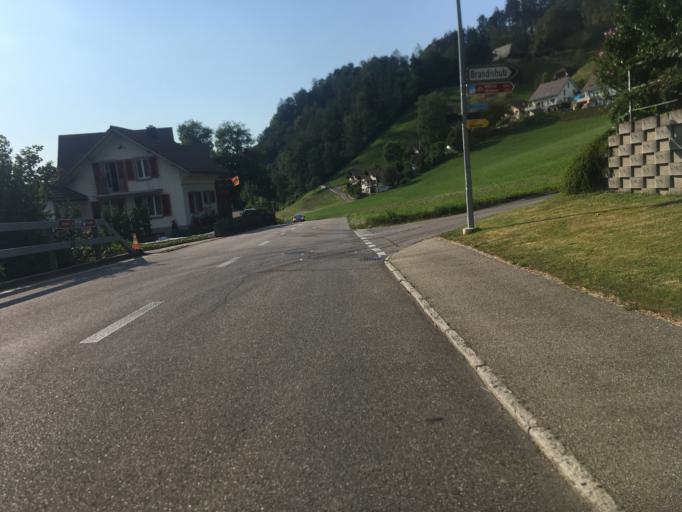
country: CH
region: Bern
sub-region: Emmental District
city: Lutzelfluh
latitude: 47.0091
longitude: 7.6835
